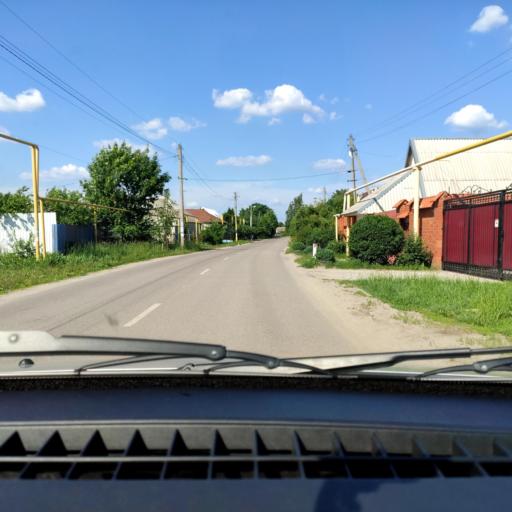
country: RU
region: Voronezj
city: Ramon'
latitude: 51.8174
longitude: 39.2655
